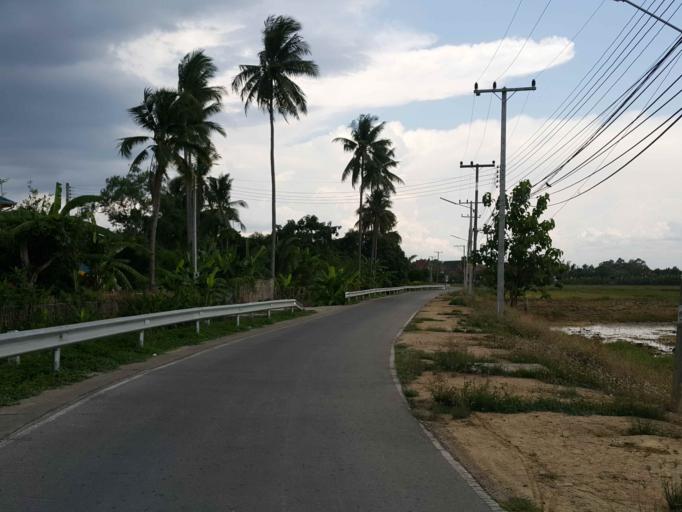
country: TH
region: Chiang Mai
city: Saraphi
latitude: 18.7084
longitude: 99.0327
